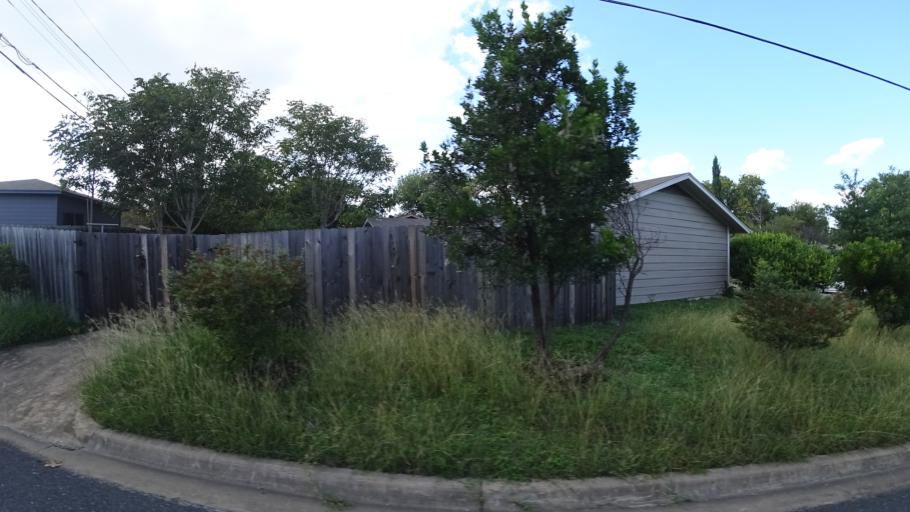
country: US
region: Texas
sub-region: Travis County
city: Wells Branch
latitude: 30.3561
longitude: -97.7078
